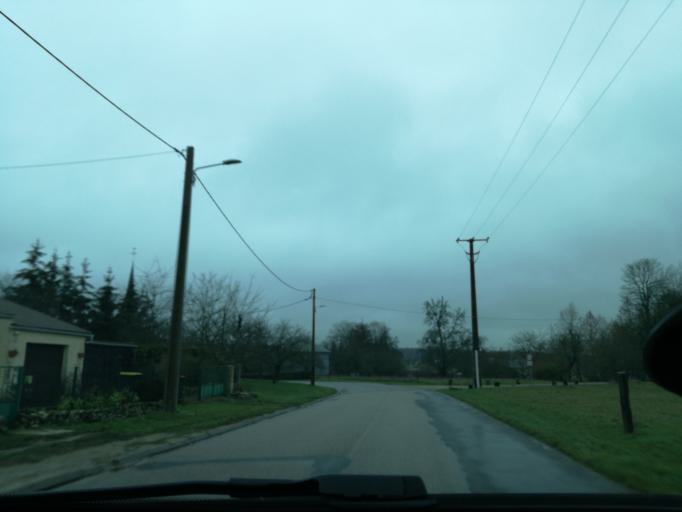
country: FR
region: Lorraine
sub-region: Departement de la Meuse
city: Clermont-en-Argonne
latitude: 49.0184
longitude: 5.1047
